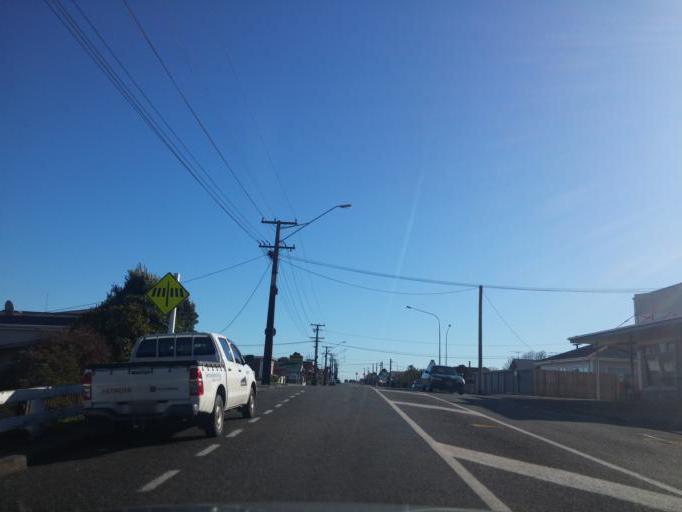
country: NZ
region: West Coast
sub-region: Grey District
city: Greymouth
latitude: -42.4428
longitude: 171.2121
